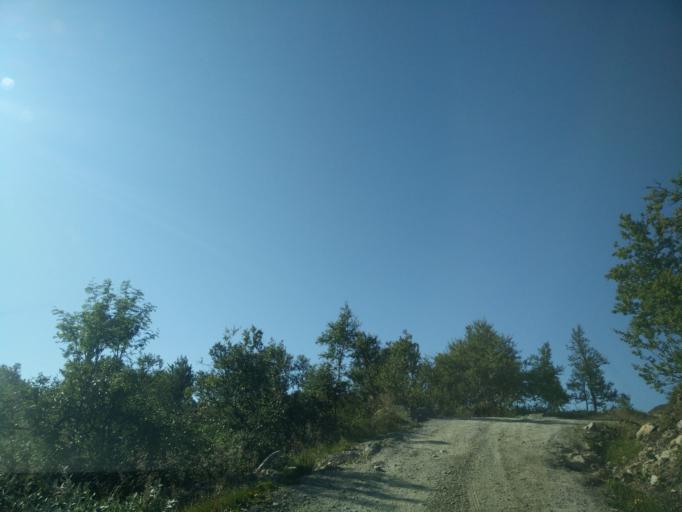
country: NO
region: Sor-Trondelag
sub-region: Tydal
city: Aas
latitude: 62.5747
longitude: 12.2008
